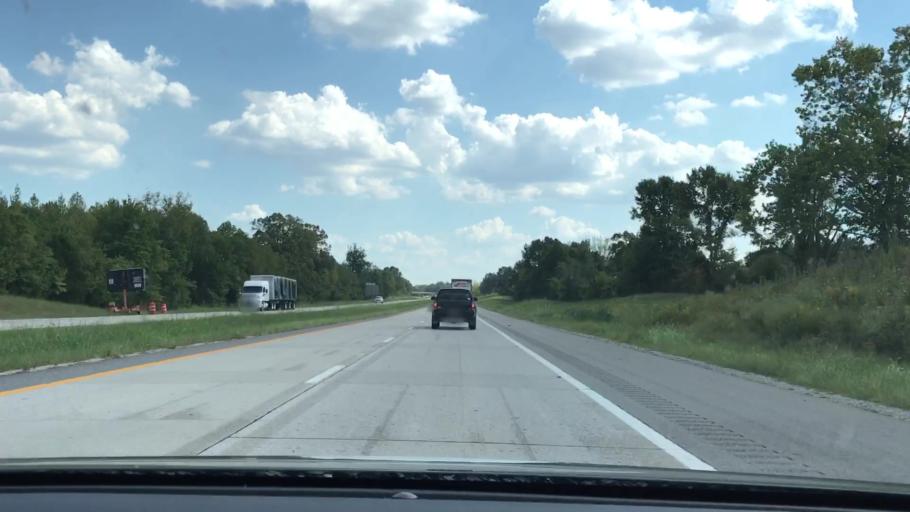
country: US
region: Kentucky
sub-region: Ohio County
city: Oak Grove
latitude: 37.3606
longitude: -86.7934
